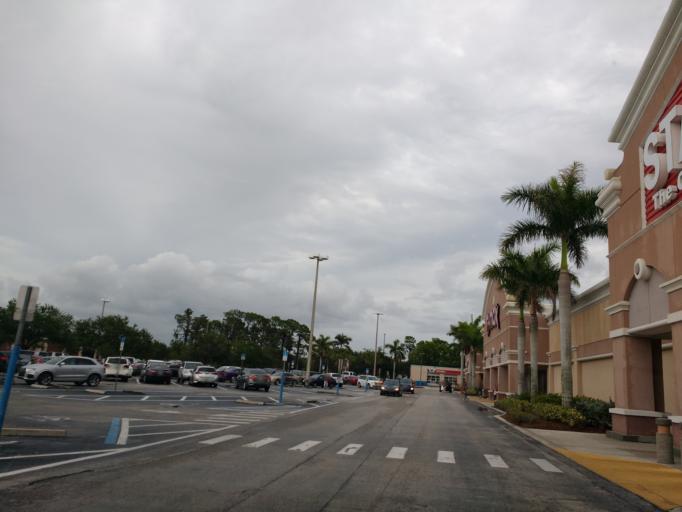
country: US
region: Florida
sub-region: Lee County
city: Villas
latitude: 26.5436
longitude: -81.8736
